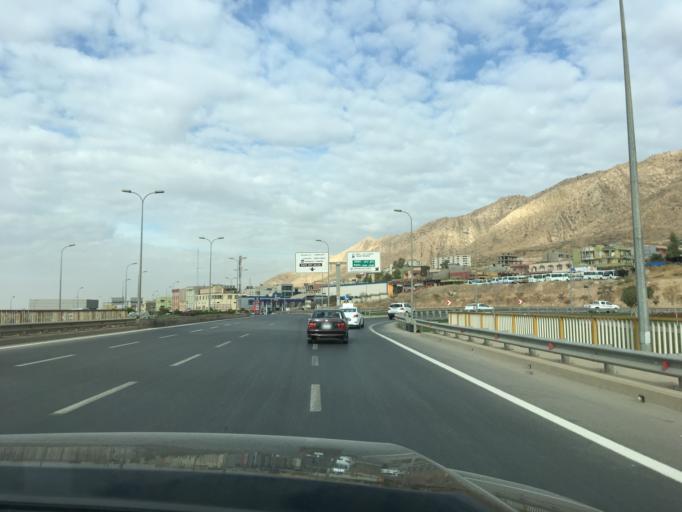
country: IQ
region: Dahuk
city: Sinah
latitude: 36.8511
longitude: 43.0507
